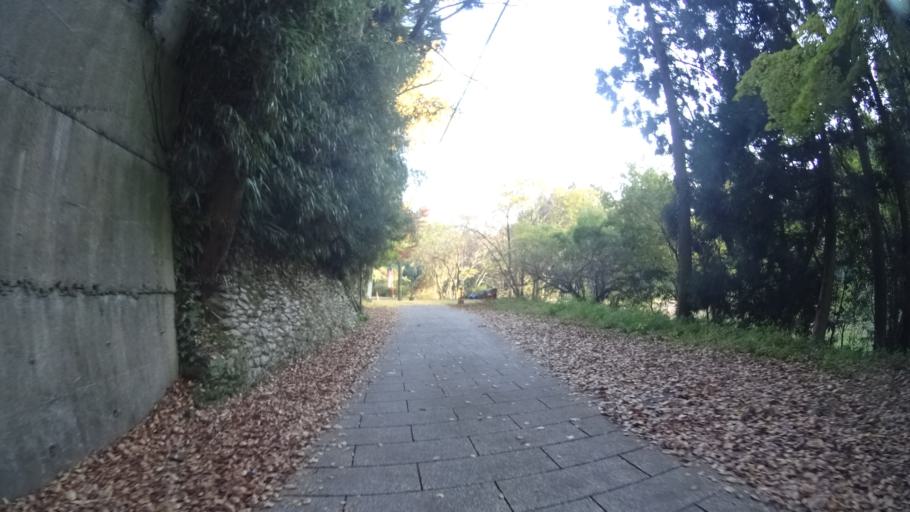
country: JP
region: Ishikawa
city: Nanao
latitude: 37.0501
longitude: 136.9534
